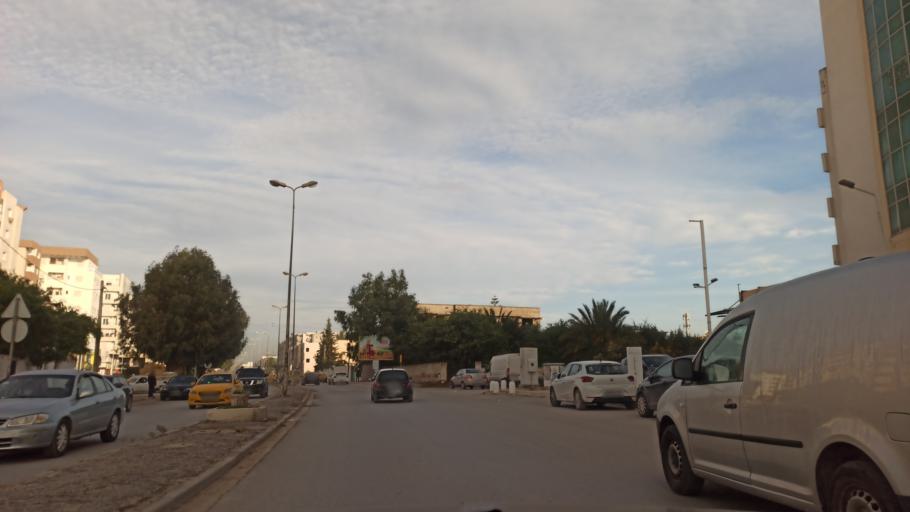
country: TN
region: Ariana
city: Ariana
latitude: 36.8593
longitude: 10.2559
